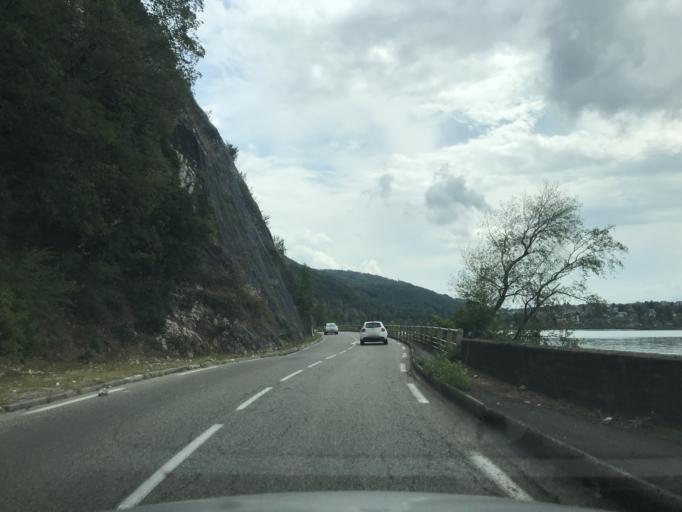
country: FR
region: Rhone-Alpes
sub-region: Departement de la Savoie
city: Brison-Saint-Innocent
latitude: 45.7430
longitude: 5.8887
